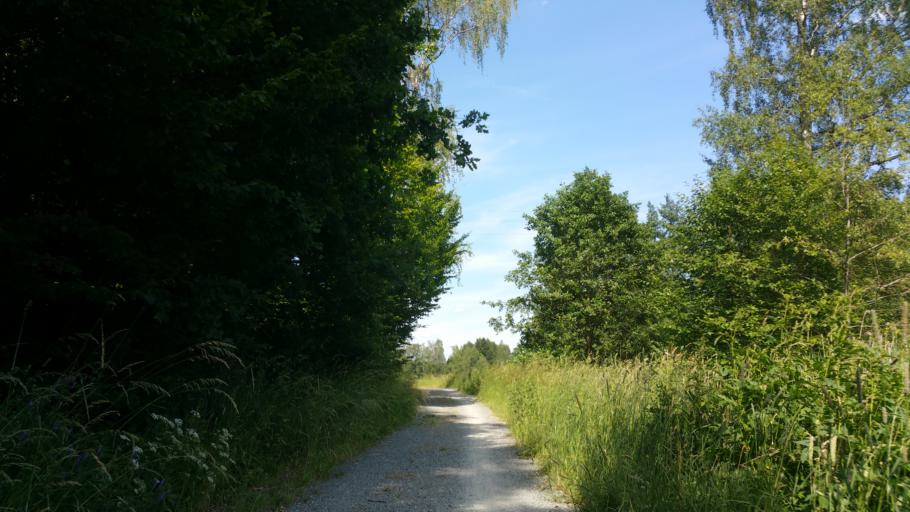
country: DE
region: Bavaria
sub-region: Upper Franconia
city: Schwarzenbach an der Saale
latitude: 50.2155
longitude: 11.9238
